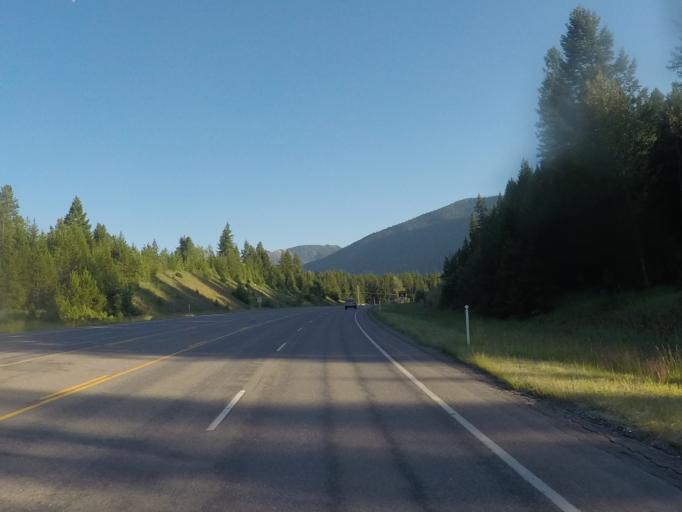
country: US
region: Montana
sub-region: Flathead County
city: Columbia Falls
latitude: 48.3937
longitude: -114.0408
